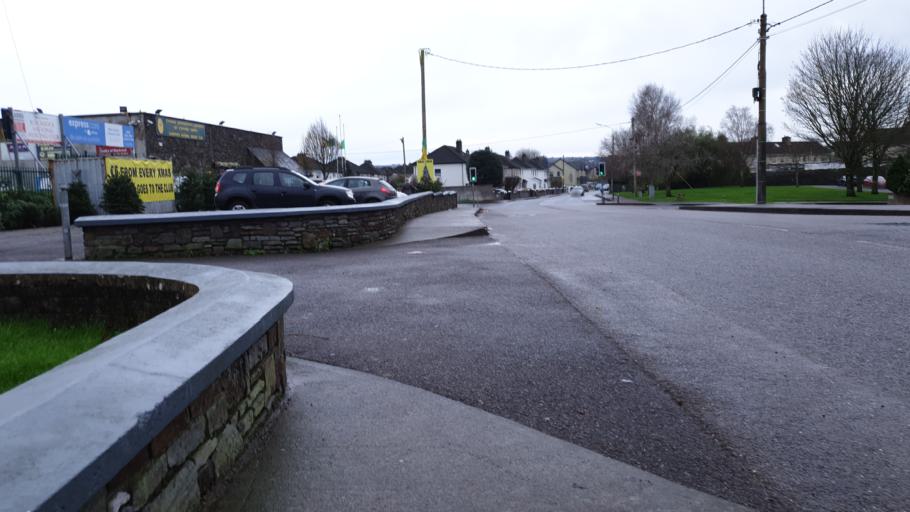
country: IE
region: Munster
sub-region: County Cork
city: Cork
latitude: 51.8930
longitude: -8.4196
